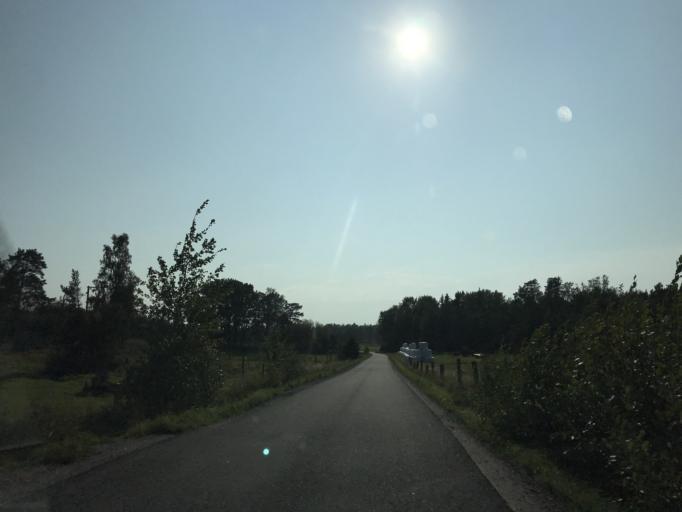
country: SE
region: Stockholm
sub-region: Norrtalje Kommun
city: Bjorko
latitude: 59.8562
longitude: 19.0211
